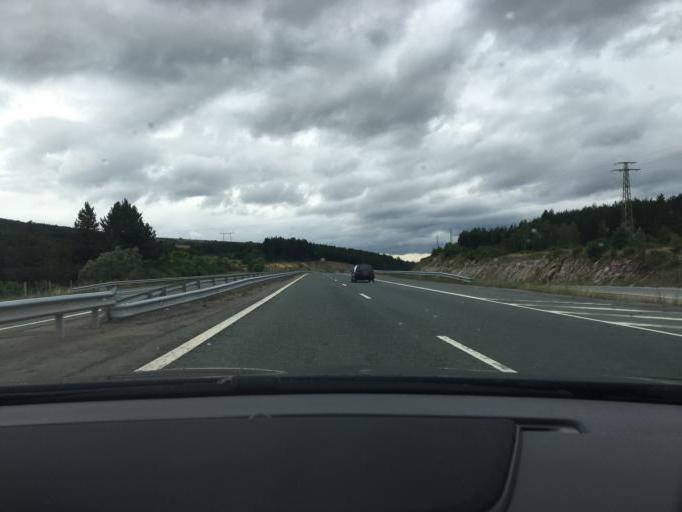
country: BG
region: Pernik
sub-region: Obshtina Pernik
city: Pernik
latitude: 42.5023
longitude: 23.1400
